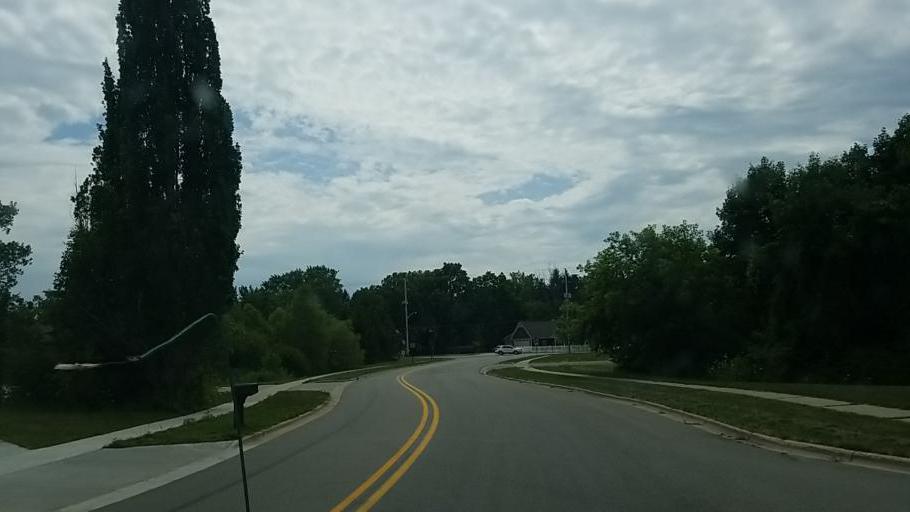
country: US
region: Michigan
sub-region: Kent County
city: Walker
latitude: 43.0011
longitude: -85.7649
